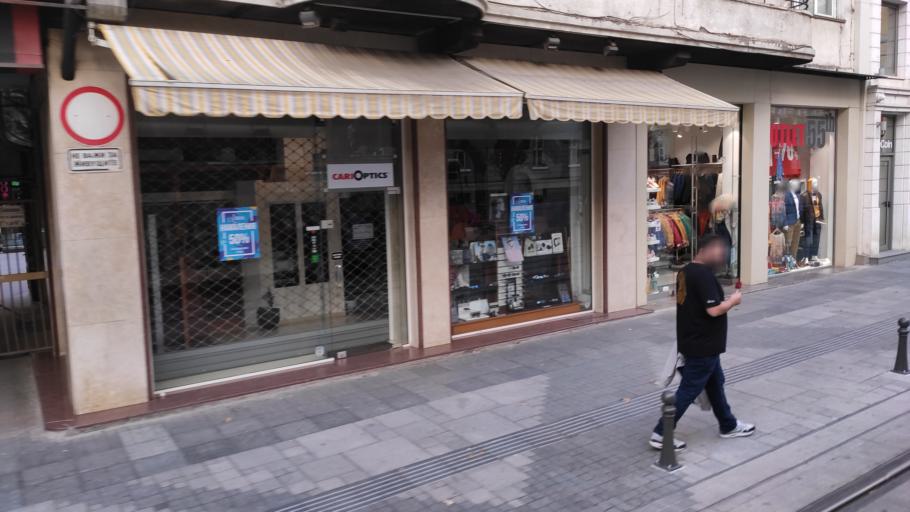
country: BG
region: Sofia-Capital
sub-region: Stolichna Obshtina
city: Sofia
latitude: 42.6919
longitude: 23.3245
